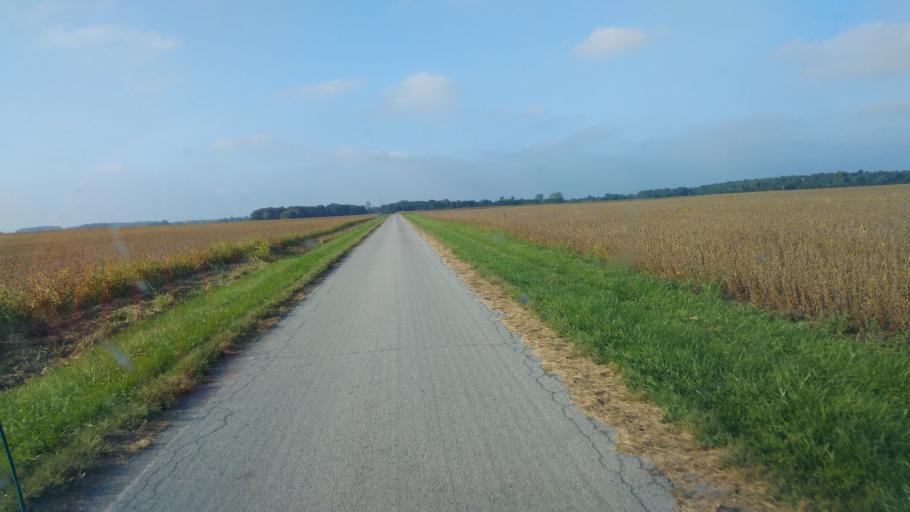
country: US
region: Ohio
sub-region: Wyandot County
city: Upper Sandusky
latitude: 40.7562
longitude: -83.2408
